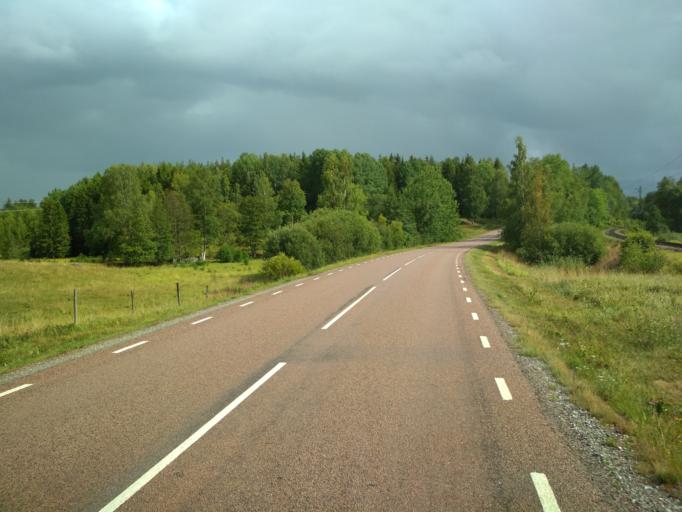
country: SE
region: Vaestmanland
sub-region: Surahammars Kommun
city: Ramnas
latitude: 59.8300
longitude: 16.1392
